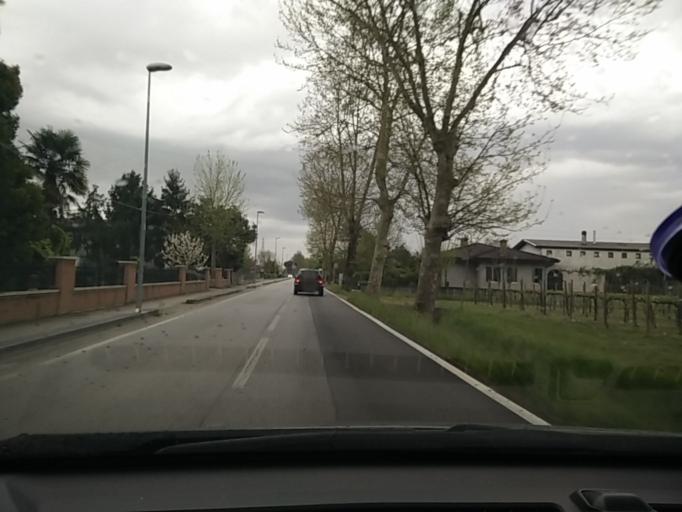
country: IT
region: Veneto
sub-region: Provincia di Venezia
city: Fossalta di Piave
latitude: 45.6458
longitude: 12.4815
